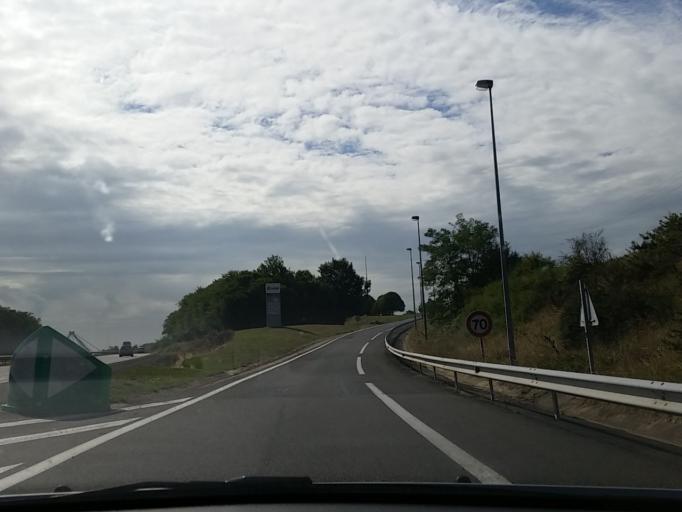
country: FR
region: Centre
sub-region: Departement du Cher
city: Orval
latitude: 46.7561
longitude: 2.4118
